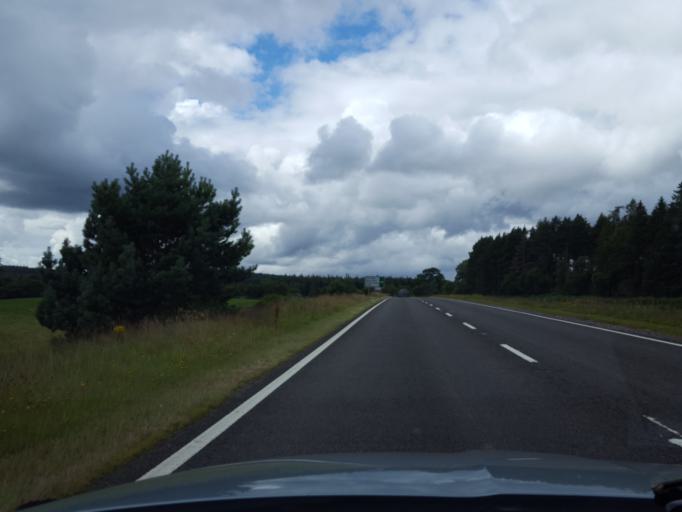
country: GB
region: Scotland
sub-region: Highland
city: Grantown on Spey
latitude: 57.3056
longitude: -3.6499
